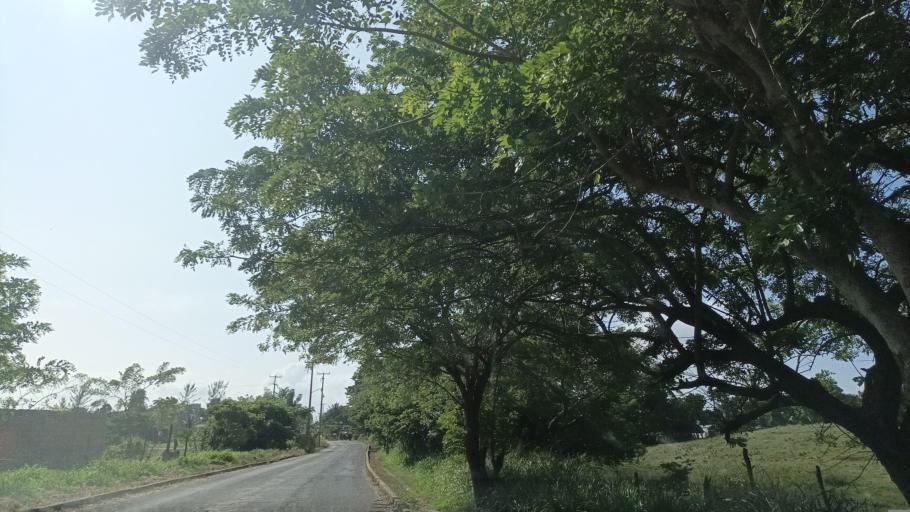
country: MX
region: Veracruz
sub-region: Pajapan
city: Pajapan
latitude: 18.2182
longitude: -94.6149
